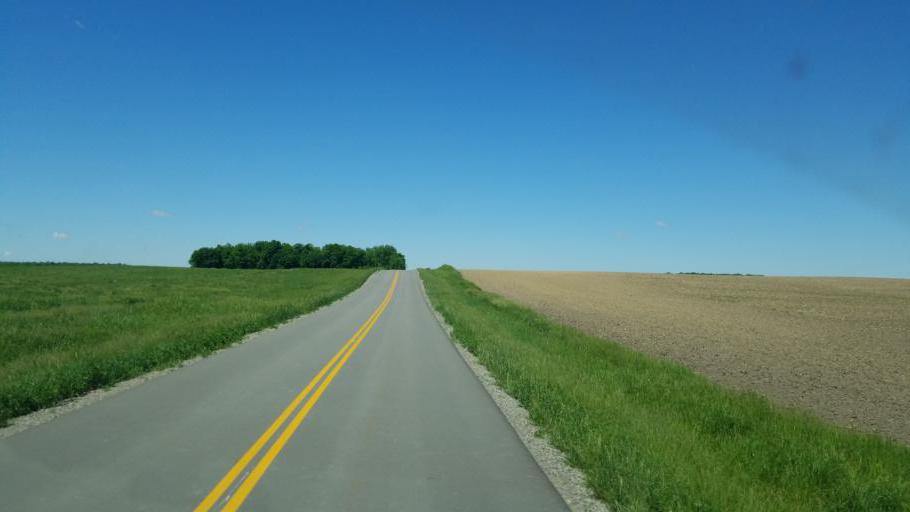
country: US
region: Ohio
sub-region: Logan County
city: Russells Point
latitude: 40.4175
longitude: -83.9294
